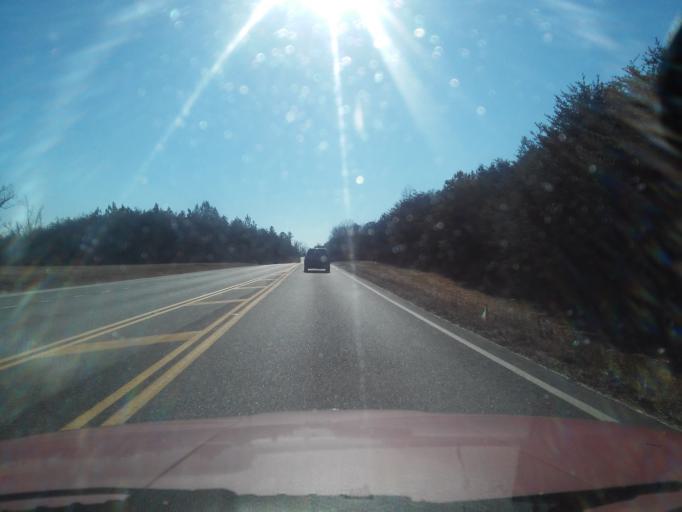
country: US
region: Virginia
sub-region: Orange County
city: Gordonsville
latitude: 37.9942
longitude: -78.1988
